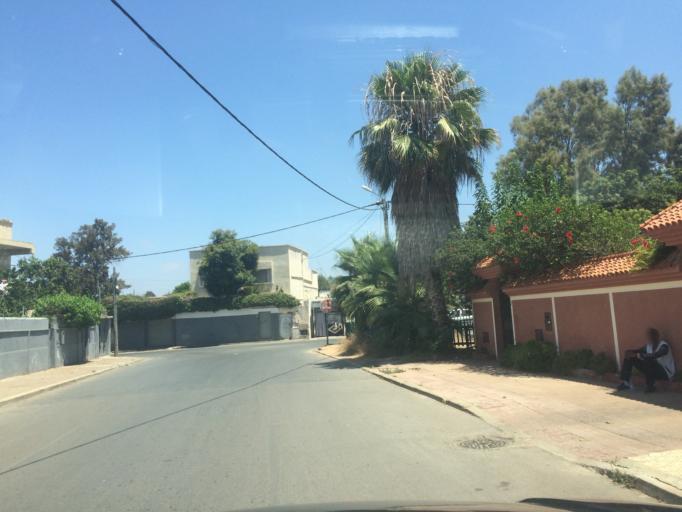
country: MA
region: Rabat-Sale-Zemmour-Zaer
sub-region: Rabat
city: Rabat
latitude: 33.9902
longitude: -6.8230
